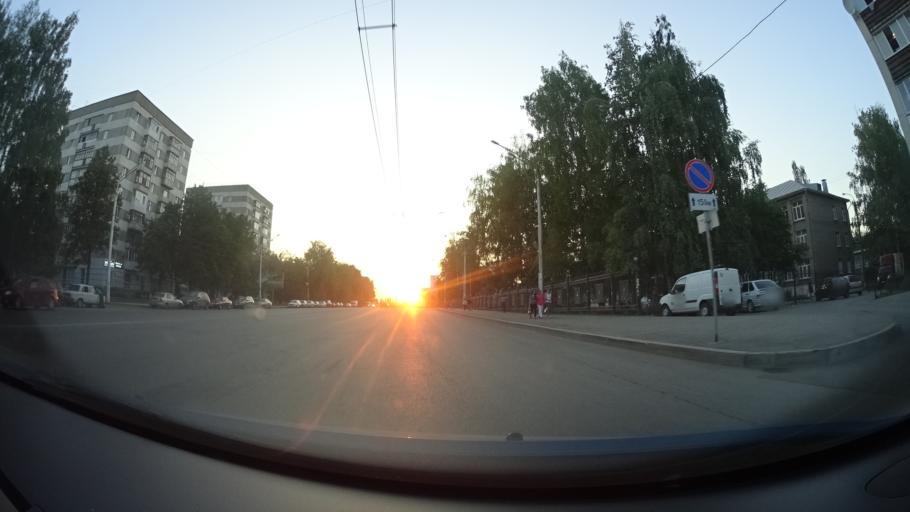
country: RU
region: Bashkortostan
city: Ufa
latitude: 54.7476
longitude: 55.9905
